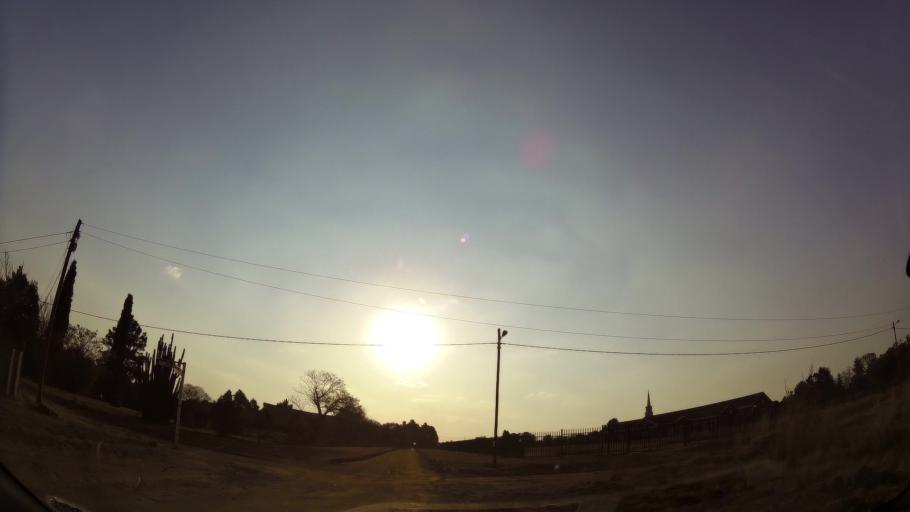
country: ZA
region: Gauteng
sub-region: Ekurhuleni Metropolitan Municipality
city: Benoni
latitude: -26.1527
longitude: 28.3663
